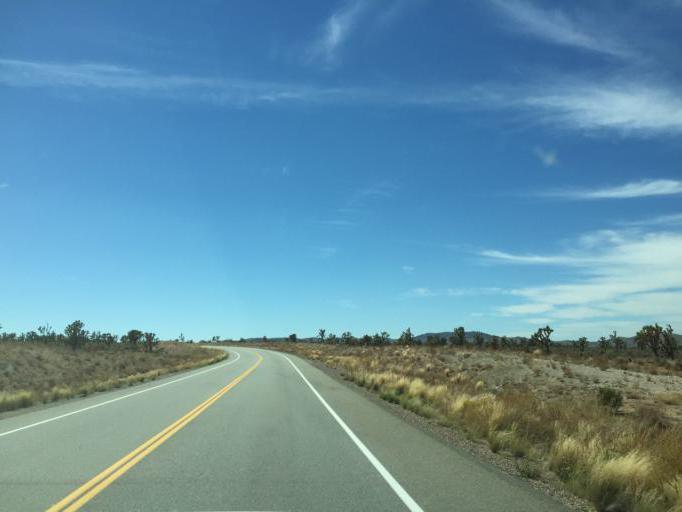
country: US
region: Arizona
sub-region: Mohave County
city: Meadview
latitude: 35.8914
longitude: -114.0339
